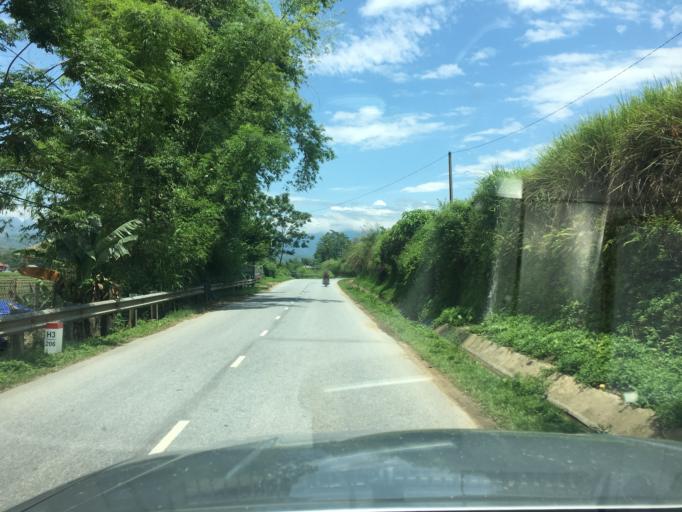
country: VN
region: Yen Bai
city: Son Thinh
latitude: 21.6293
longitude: 104.5063
